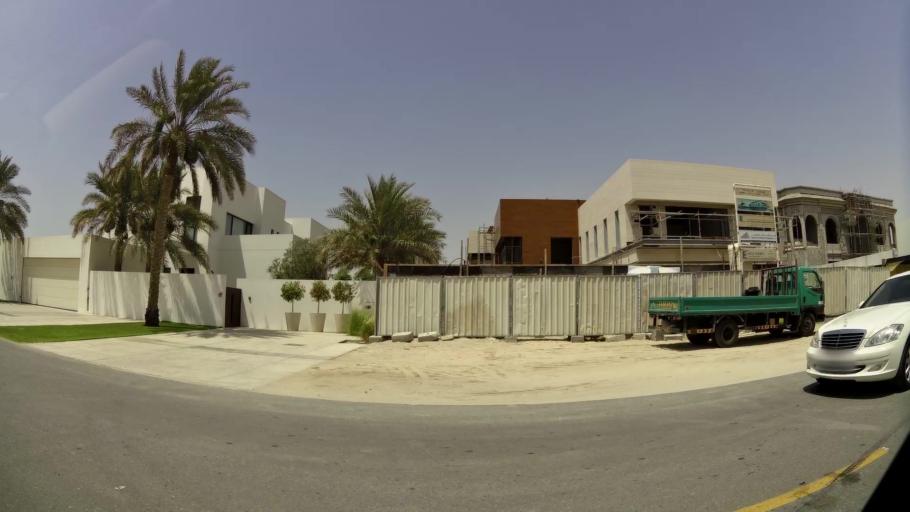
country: AE
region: Dubai
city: Dubai
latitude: 25.1345
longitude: 55.2039
